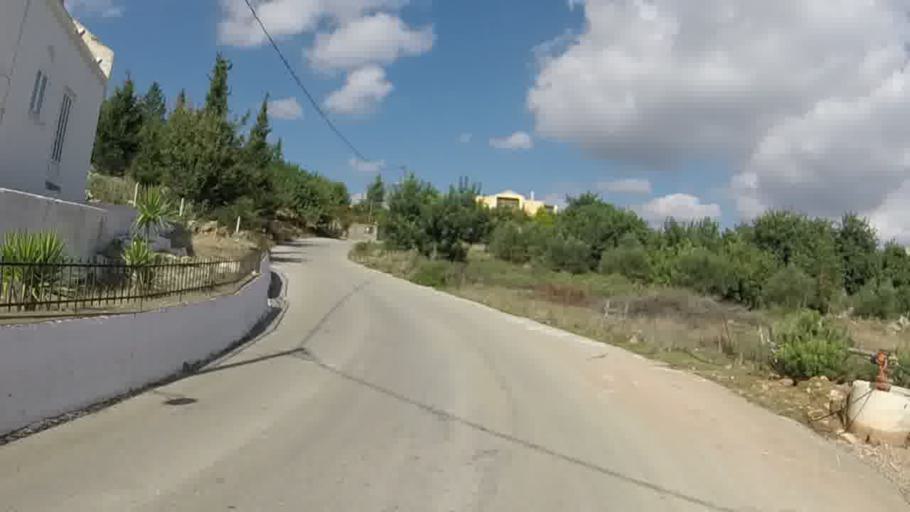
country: GR
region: Crete
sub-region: Nomos Chanias
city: Kalivai
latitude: 35.3885
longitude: 24.1322
